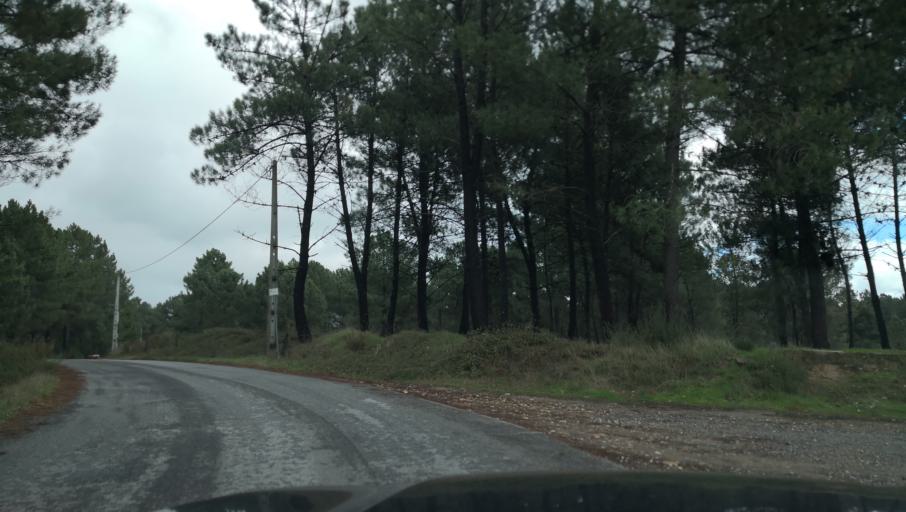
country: PT
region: Vila Real
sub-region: Vila Real
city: Vila Real
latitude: 41.3164
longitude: -7.7540
